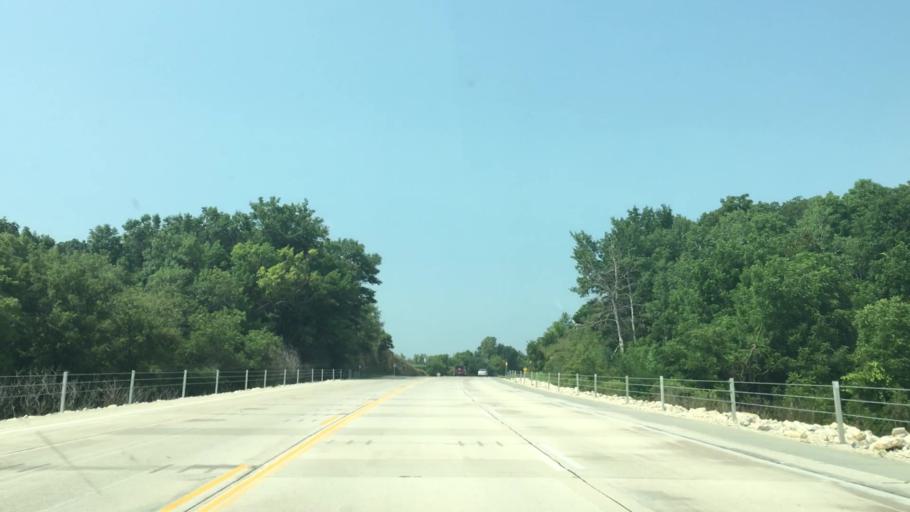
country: US
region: Iowa
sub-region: Winneshiek County
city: Decorah
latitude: 43.3035
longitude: -91.8146
